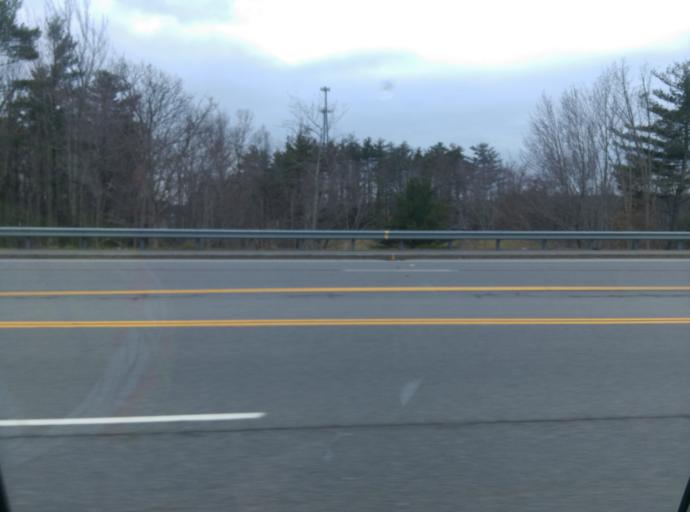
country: US
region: New Hampshire
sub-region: Rockingham County
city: Seabrook
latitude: 42.8948
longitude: -70.8810
